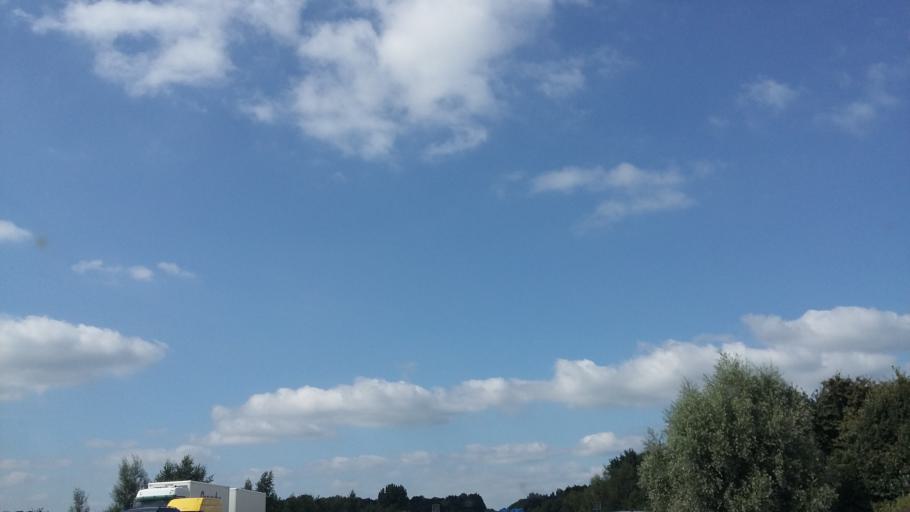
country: DE
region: Lower Saxony
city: Ritterhude
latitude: 53.1630
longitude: 8.7207
